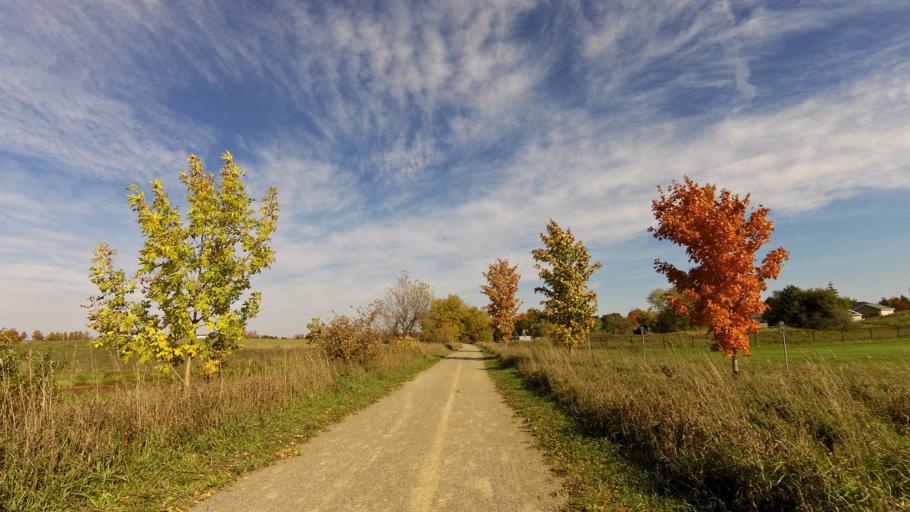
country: CA
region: Ontario
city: Orangeville
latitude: 43.7801
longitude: -80.0677
